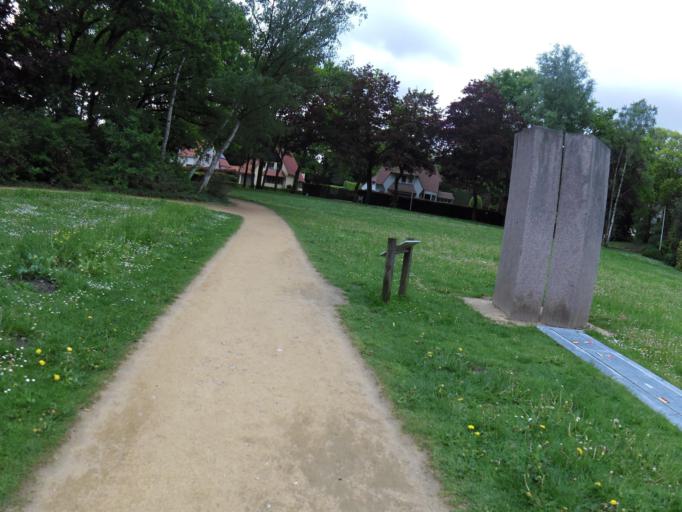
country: BE
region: Flanders
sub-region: Provincie Limburg
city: Genk
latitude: 50.9646
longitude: 5.5155
